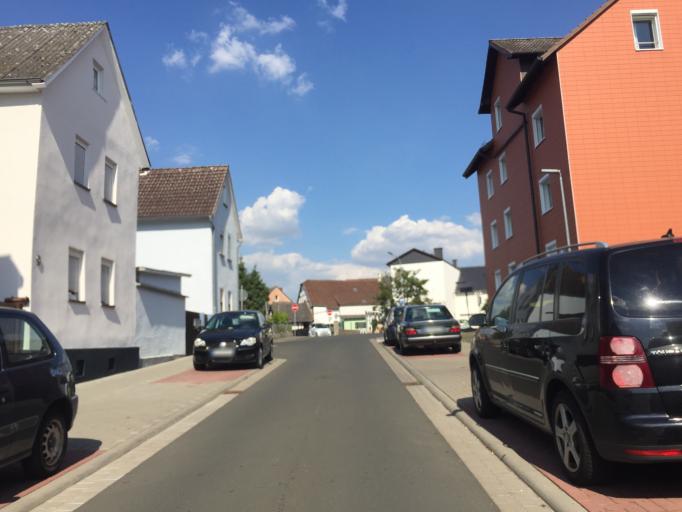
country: DE
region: Hesse
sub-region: Regierungsbezirk Giessen
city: Langgons
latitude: 50.5350
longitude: 8.7064
